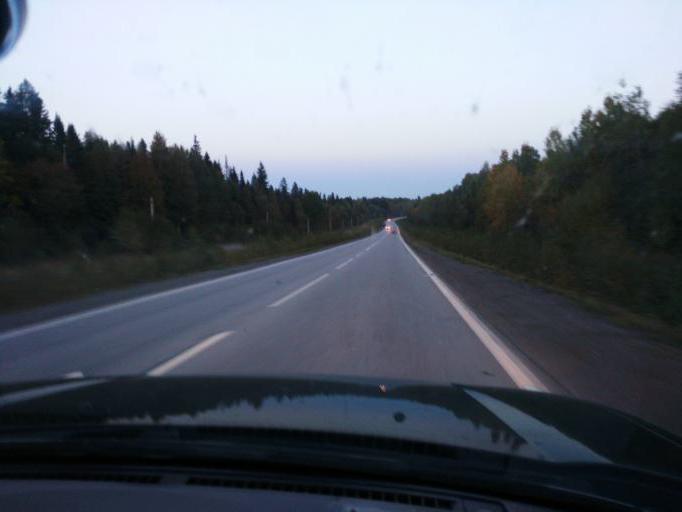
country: RU
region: Perm
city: Verkhnechusovskiye Gorodki
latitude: 58.2587
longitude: 56.9886
